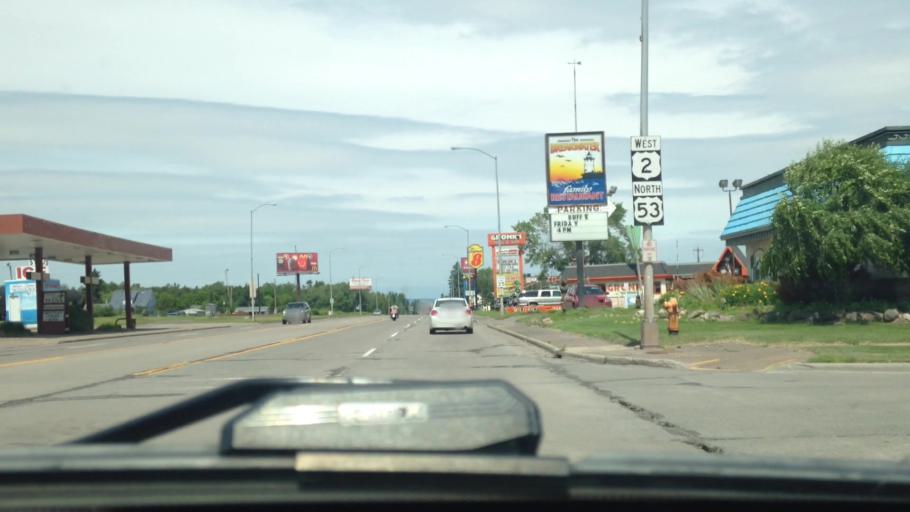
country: US
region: Wisconsin
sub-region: Douglas County
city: Superior
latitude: 46.6780
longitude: -92.0107
